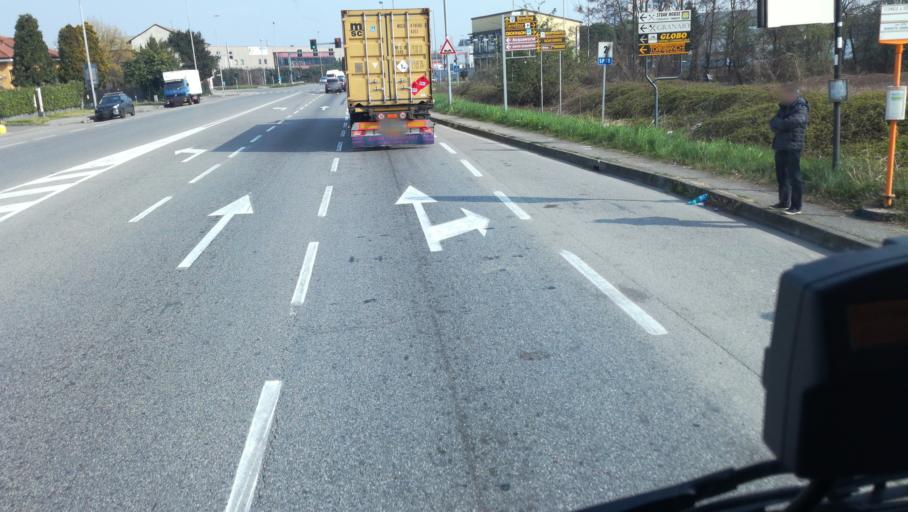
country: IT
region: Lombardy
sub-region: Provincia di Monza e Brianza
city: Concorezzo
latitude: 45.5800
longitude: 9.3227
